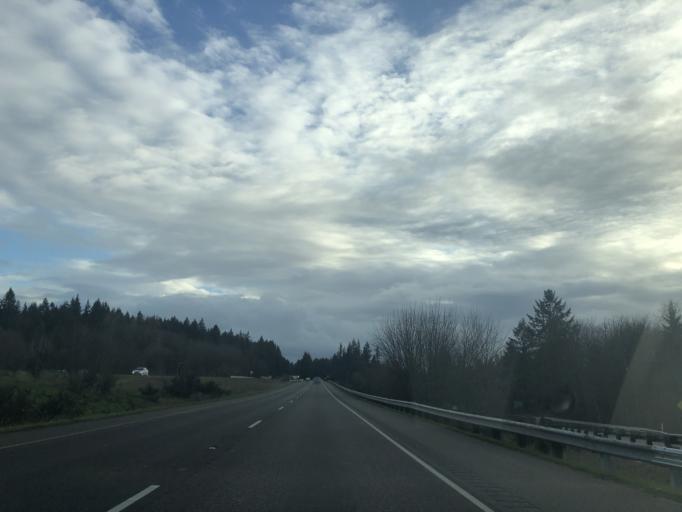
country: US
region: Washington
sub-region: Kitsap County
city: Bethel
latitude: 47.4712
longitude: -122.6247
